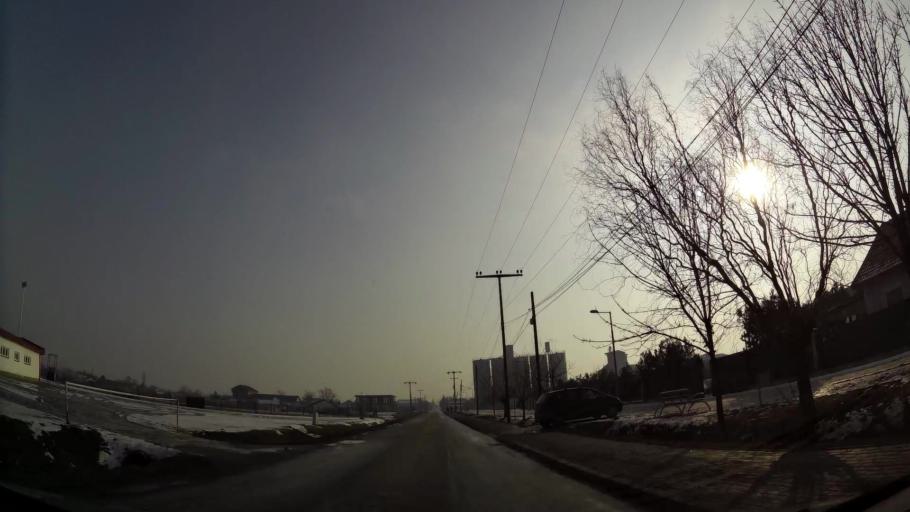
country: MK
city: Kadino
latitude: 41.9761
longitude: 21.5941
